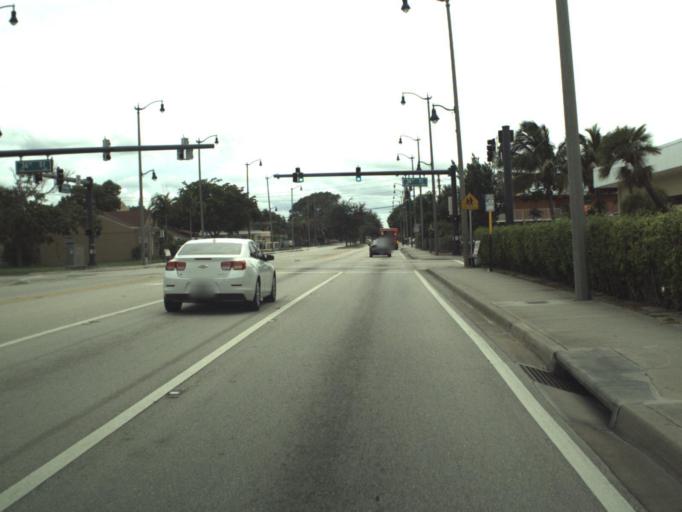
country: US
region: Florida
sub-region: Palm Beach County
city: Mangonia Park
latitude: 26.7464
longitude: -80.0566
